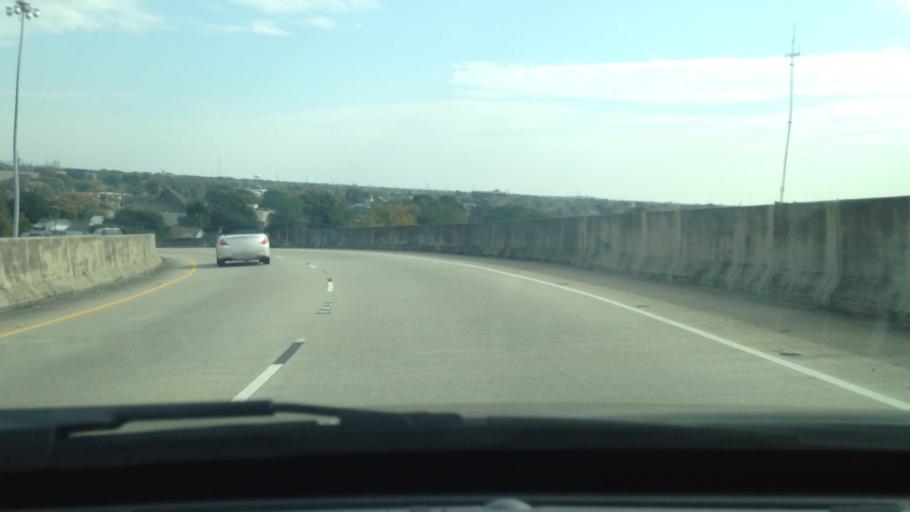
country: US
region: Louisiana
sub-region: Jefferson Parish
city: Terrytown
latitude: 29.9297
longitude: -90.0380
